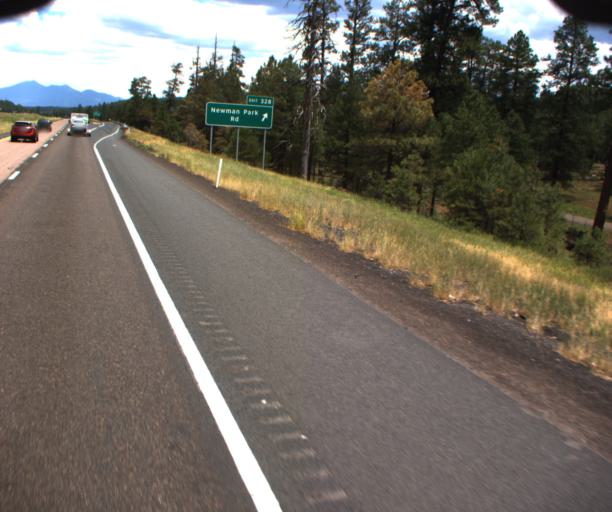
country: US
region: Arizona
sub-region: Coconino County
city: Mountainaire
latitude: 35.0137
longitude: -111.6847
